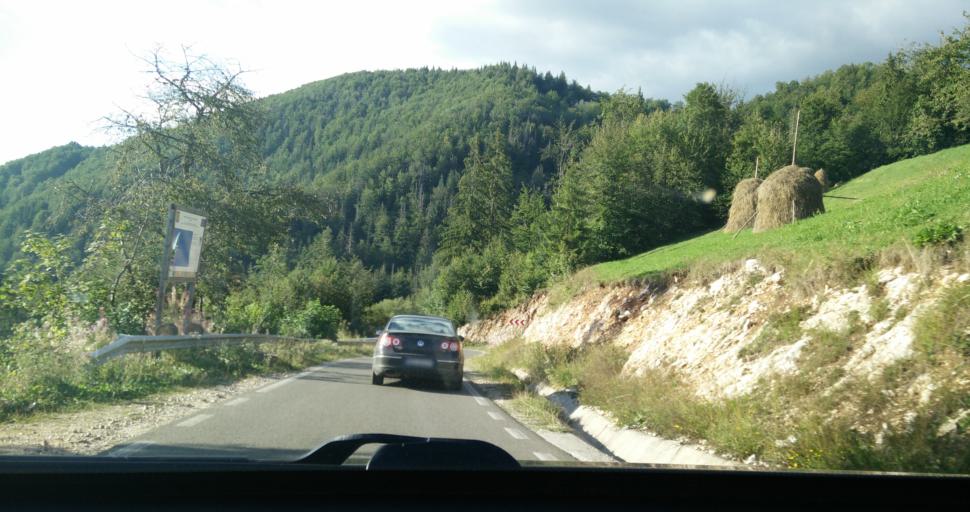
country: RO
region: Alba
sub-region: Comuna Scarisoara
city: Scarisoara
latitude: 46.4686
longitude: 22.8282
